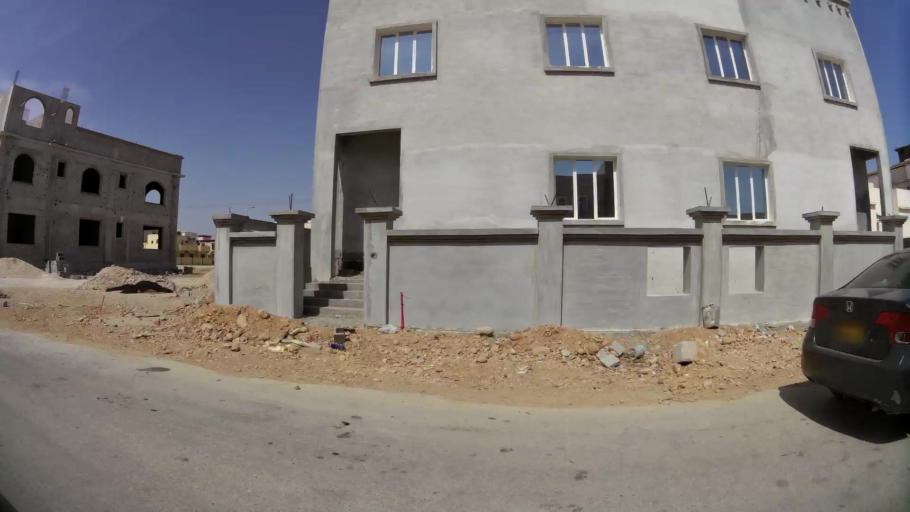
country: OM
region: Zufar
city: Salalah
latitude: 17.0469
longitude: 54.1540
